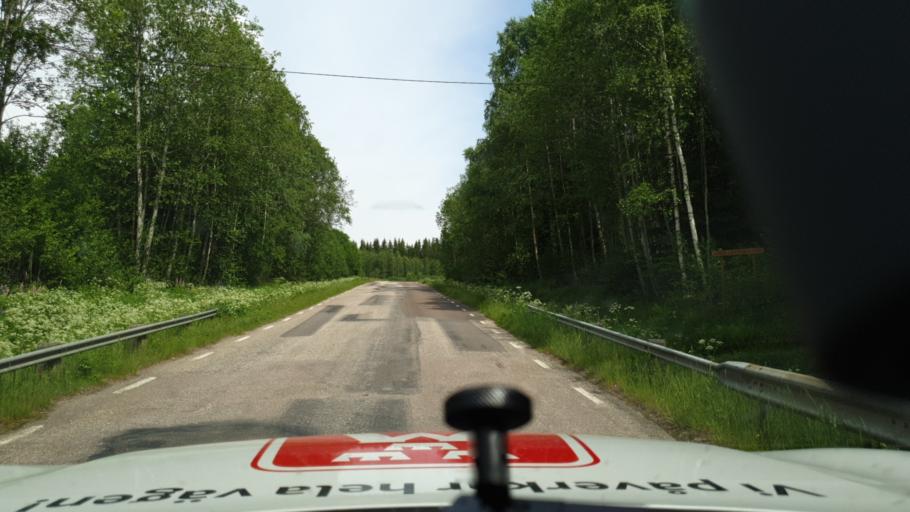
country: SE
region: Vaermland
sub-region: Torsby Kommun
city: Torsby
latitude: 59.9863
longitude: 12.8392
